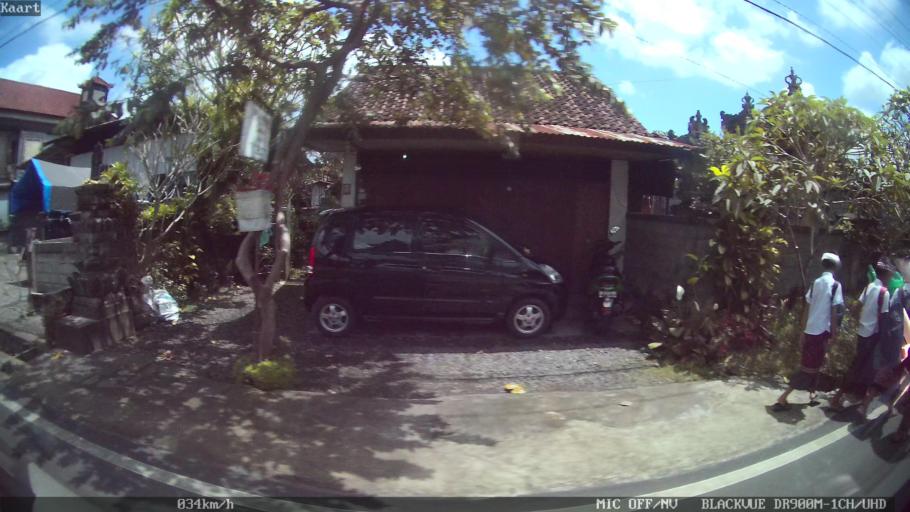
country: ID
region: Bali
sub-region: Kabupaten Gianyar
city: Ubud
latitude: -8.5316
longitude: 115.2822
